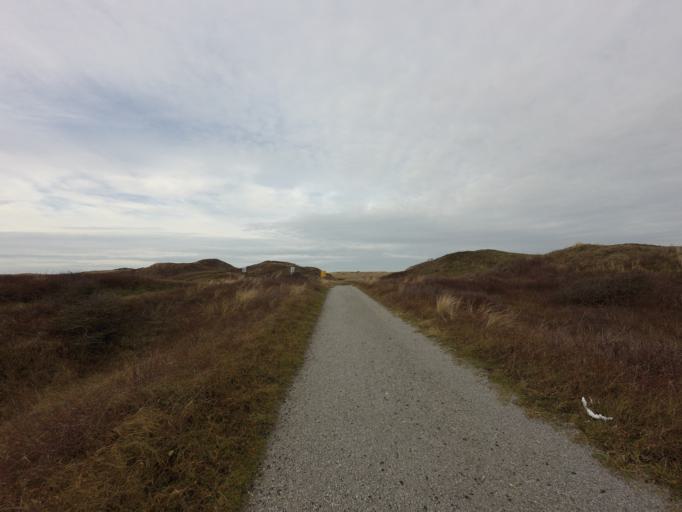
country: NL
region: North Holland
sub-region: Gemeente Texel
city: Den Burg
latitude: 53.0623
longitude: 4.7270
